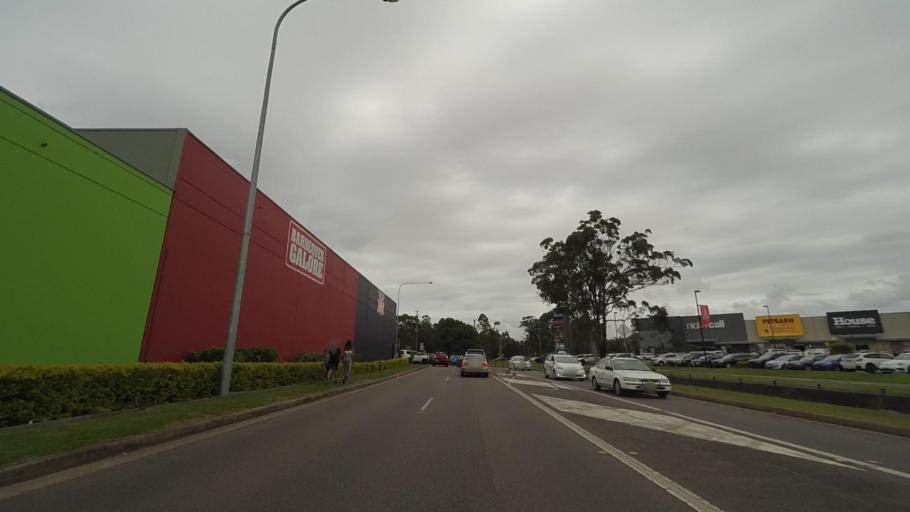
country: AU
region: New South Wales
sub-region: Lake Macquarie Shire
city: Highfields
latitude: -32.9397
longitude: 151.7077
